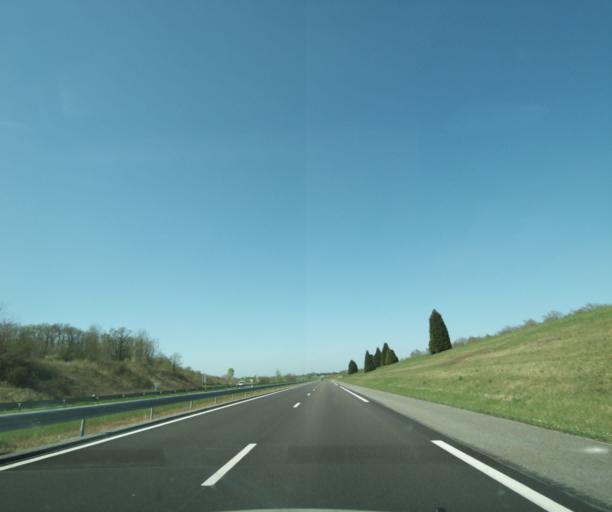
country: FR
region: Bourgogne
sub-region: Departement de la Nievre
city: Neuvy-sur-Loire
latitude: 47.5094
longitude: 2.9202
